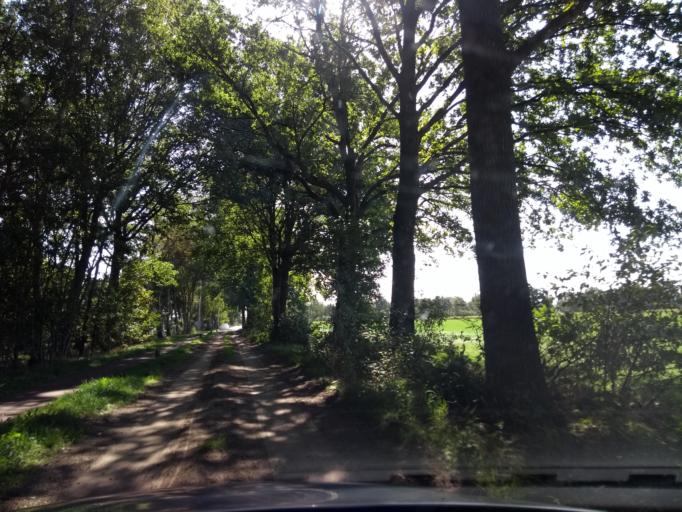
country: DE
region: Lower Saxony
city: Lage
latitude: 52.4256
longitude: 7.0038
